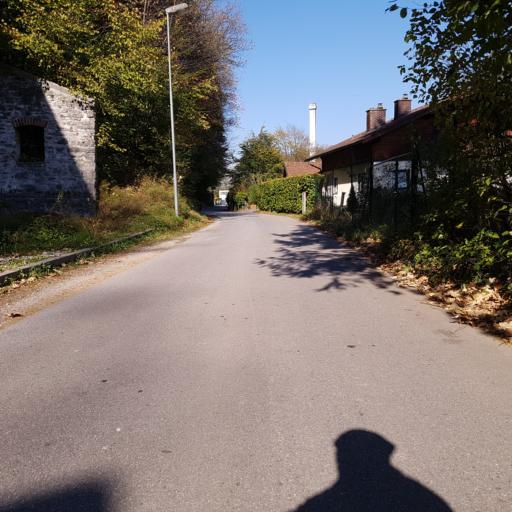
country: AT
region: Salzburg
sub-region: Politischer Bezirk Hallein
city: Hallein
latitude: 47.6685
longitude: 13.1078
